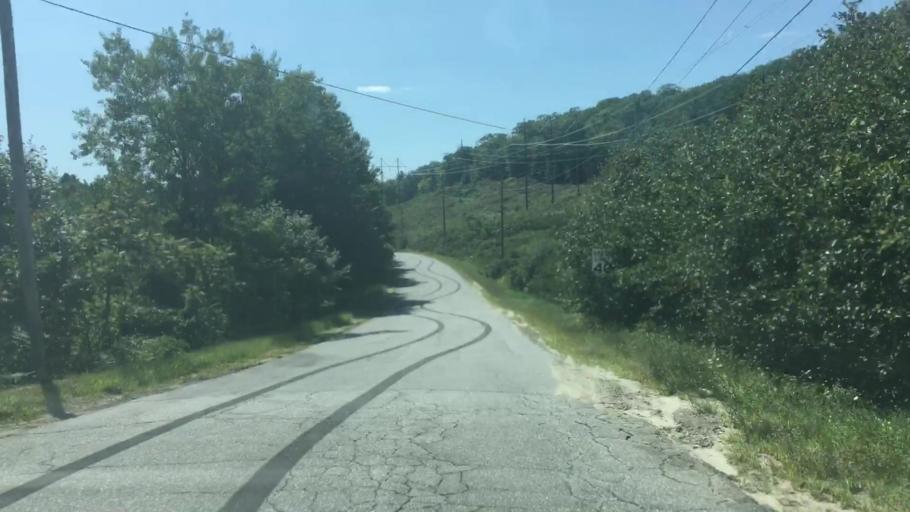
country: US
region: Maine
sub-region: Kennebec County
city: Monmouth
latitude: 44.2013
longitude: -69.9597
